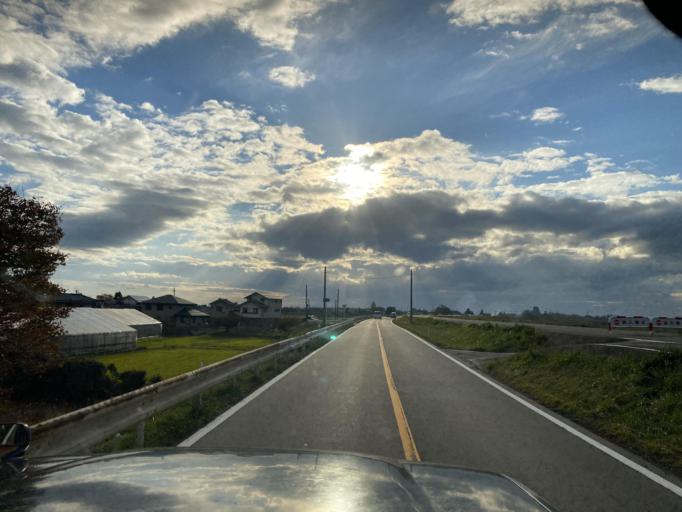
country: JP
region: Niigata
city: Kamo
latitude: 37.6852
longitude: 139.0269
